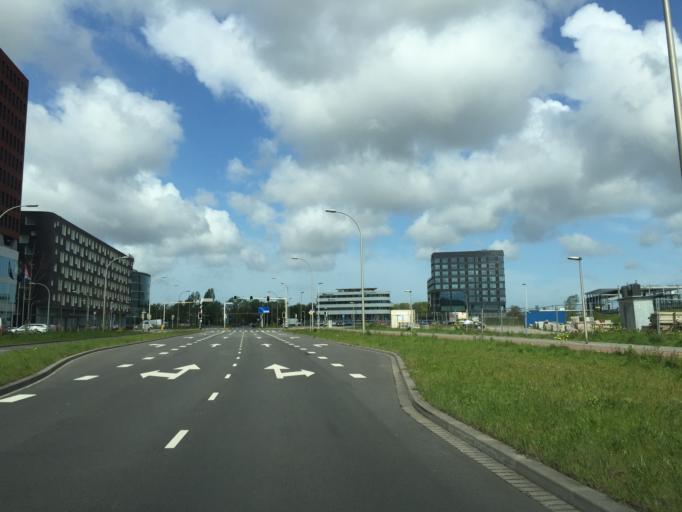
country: NL
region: South Holland
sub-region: Gemeente Den Haag
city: Ypenburg
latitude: 52.0546
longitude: 4.3928
